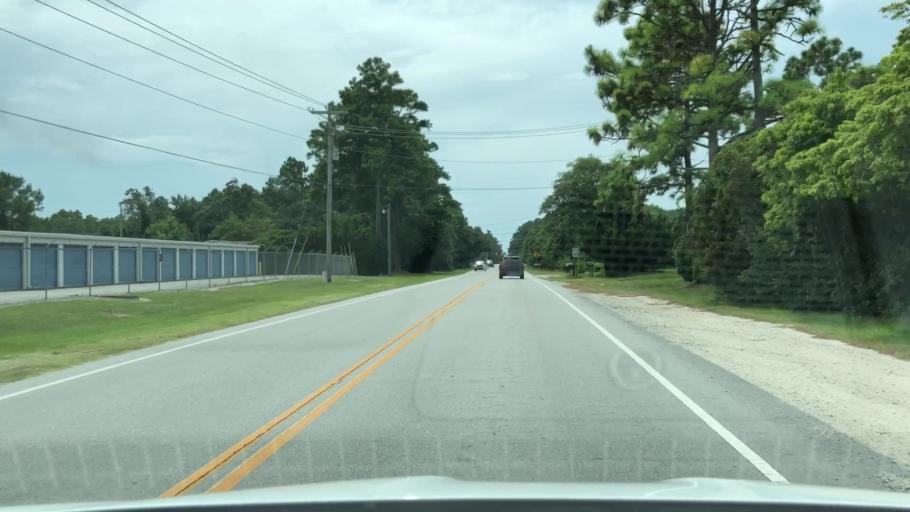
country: US
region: North Carolina
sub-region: Carteret County
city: Broad Creek
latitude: 34.7326
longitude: -76.8895
